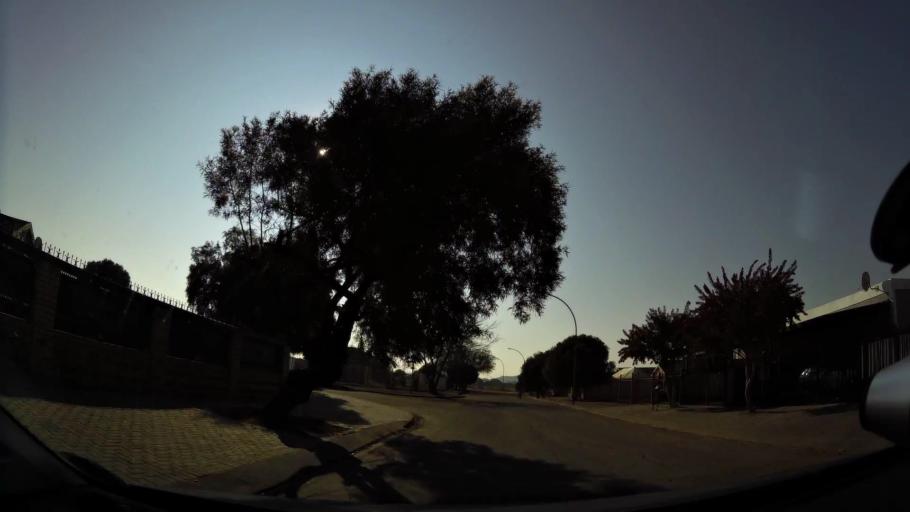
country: ZA
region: Orange Free State
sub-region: Mangaung Metropolitan Municipality
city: Bloemfontein
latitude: -29.1839
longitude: 26.1755
